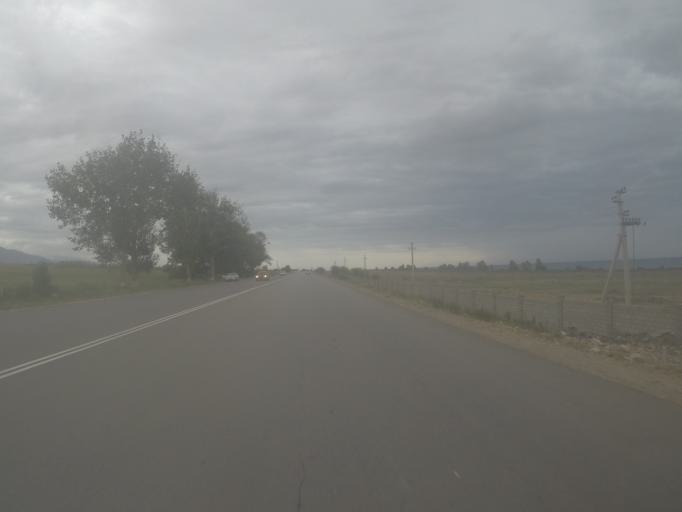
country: KG
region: Ysyk-Koel
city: Cholpon-Ata
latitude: 42.5979
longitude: 76.8046
